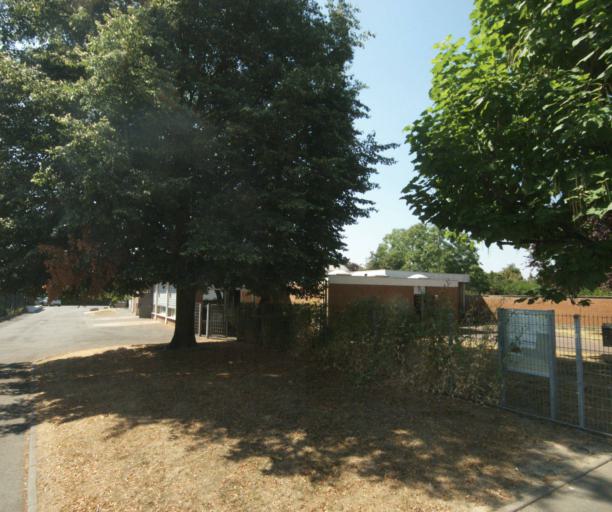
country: FR
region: Nord-Pas-de-Calais
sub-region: Departement du Nord
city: Bousbecque
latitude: 50.7703
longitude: 3.0757
